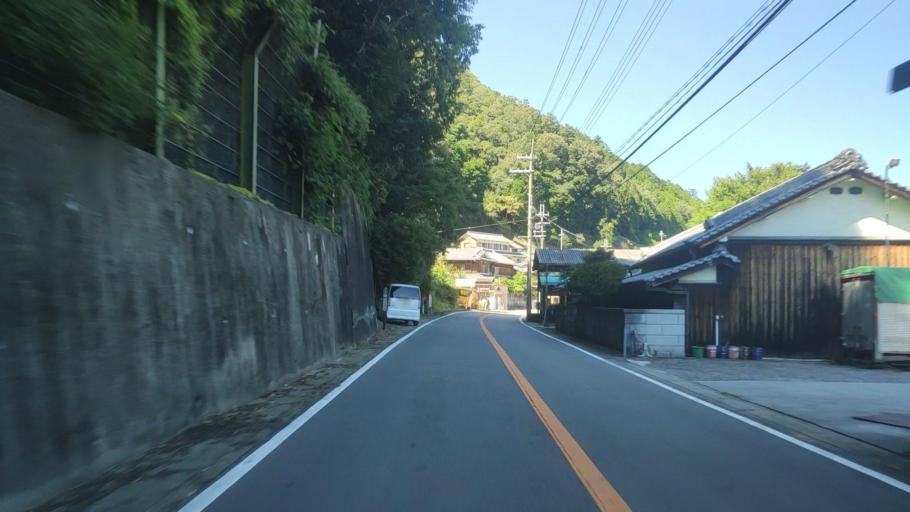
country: JP
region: Nara
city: Yoshino-cho
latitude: 34.3855
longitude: 135.9161
